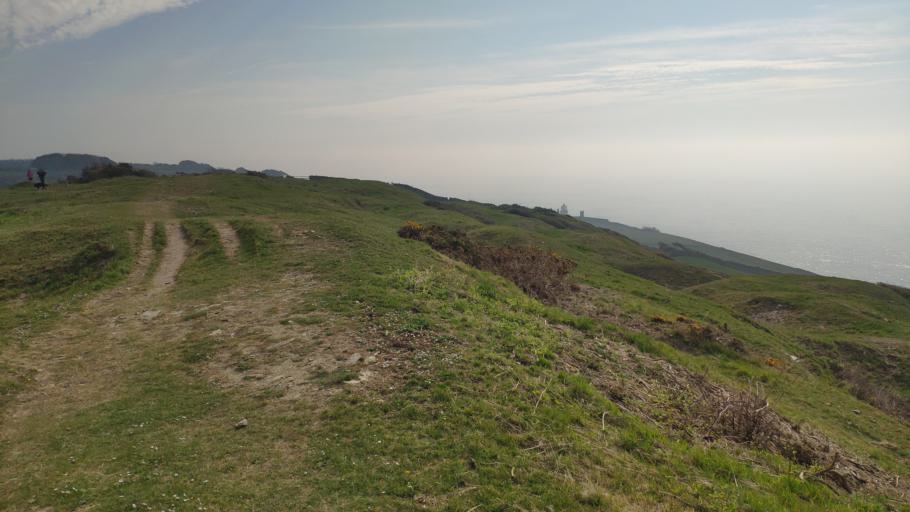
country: GB
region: England
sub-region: Dorset
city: Swanage
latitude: 50.5932
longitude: -1.9671
